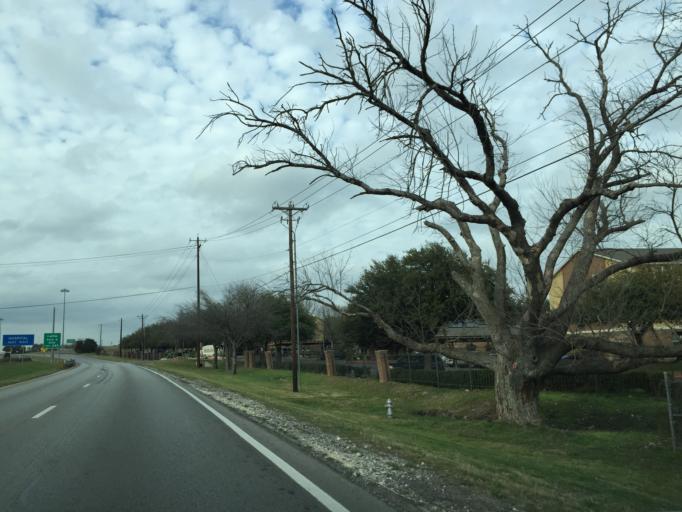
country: US
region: Texas
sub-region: Travis County
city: Wells Branch
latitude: 30.3933
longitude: -97.6712
